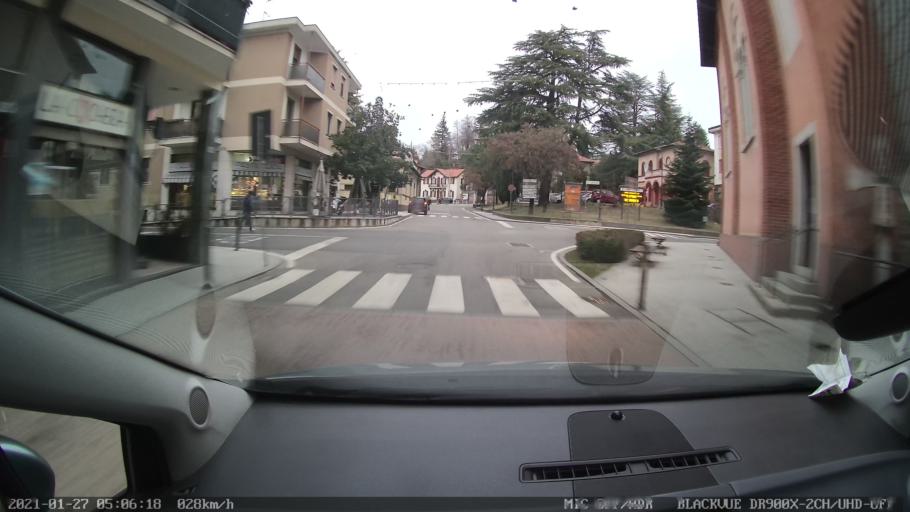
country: IT
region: Lombardy
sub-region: Provincia di Varese
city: Tradate
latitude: 45.7036
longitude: 8.9208
